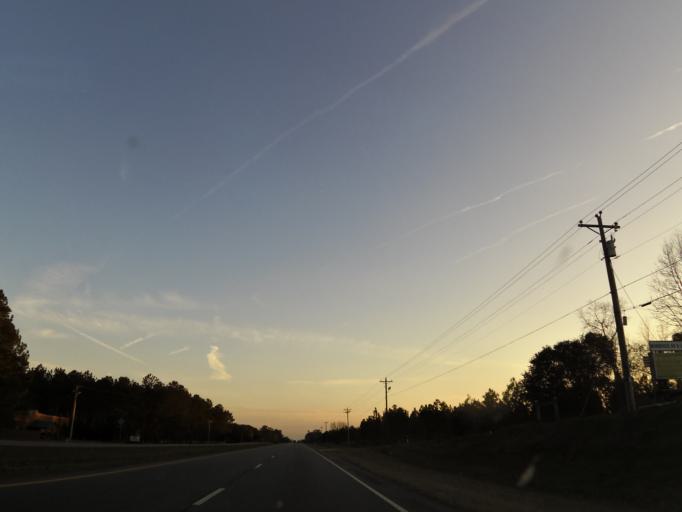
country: US
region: Georgia
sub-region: Lee County
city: Leesburg
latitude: 31.7143
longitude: -84.1726
